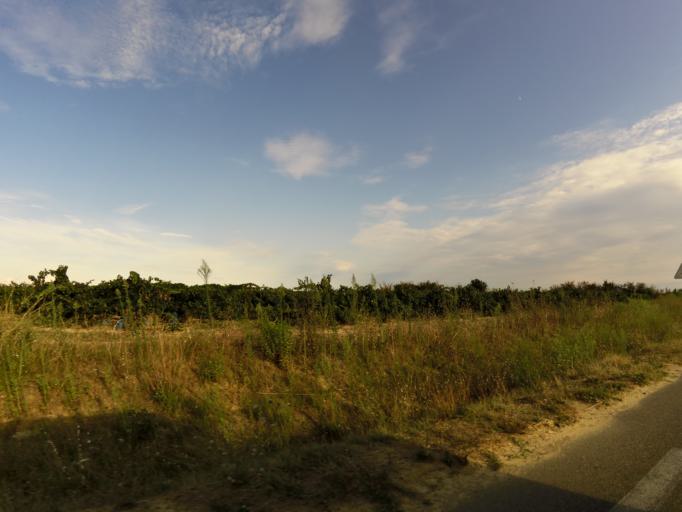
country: FR
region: Languedoc-Roussillon
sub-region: Departement du Gard
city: Gallargues-le-Montueux
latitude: 43.6997
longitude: 4.1675
